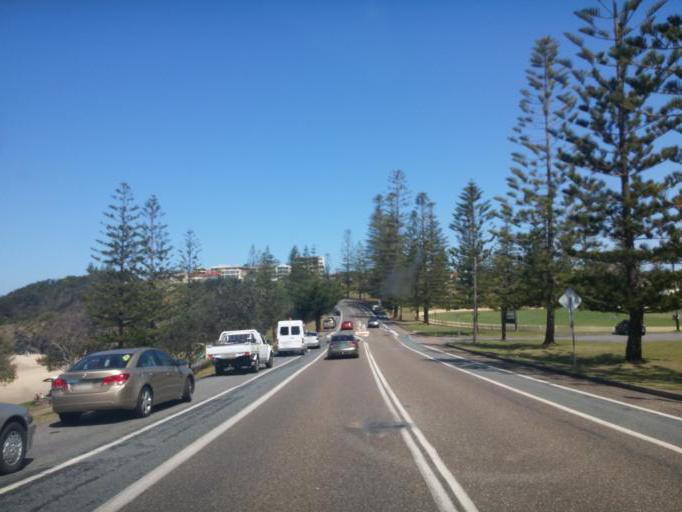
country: AU
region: New South Wales
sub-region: Port Macquarie-Hastings
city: Port Macquarie
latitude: -31.4310
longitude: 152.9225
